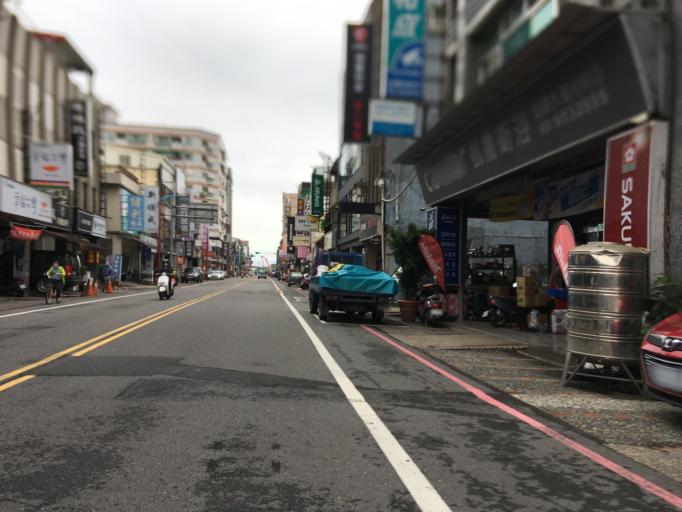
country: TW
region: Taiwan
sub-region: Yilan
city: Yilan
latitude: 24.6826
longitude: 121.7699
